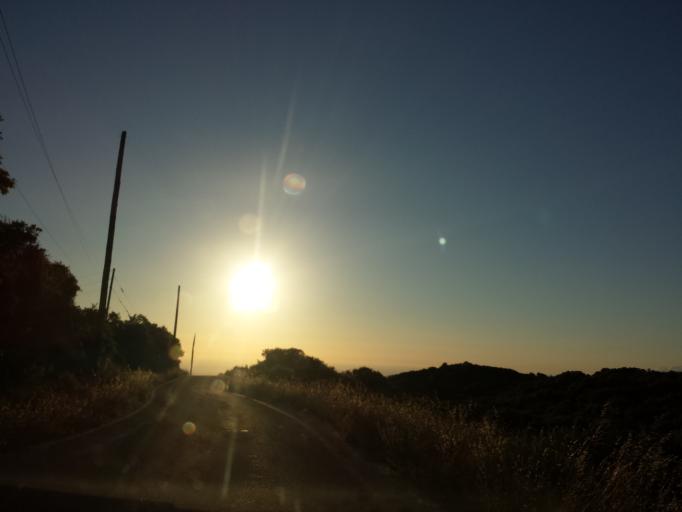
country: GR
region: Ionian Islands
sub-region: Nomos Kerkyras
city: Acharavi
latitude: 39.7522
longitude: 19.8472
